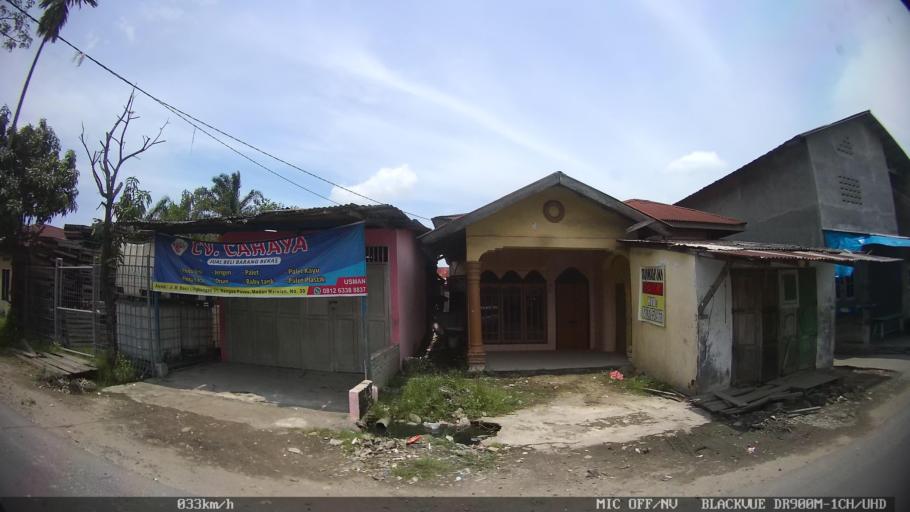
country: ID
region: North Sumatra
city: Labuhan Deli
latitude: 3.7091
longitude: 98.6735
